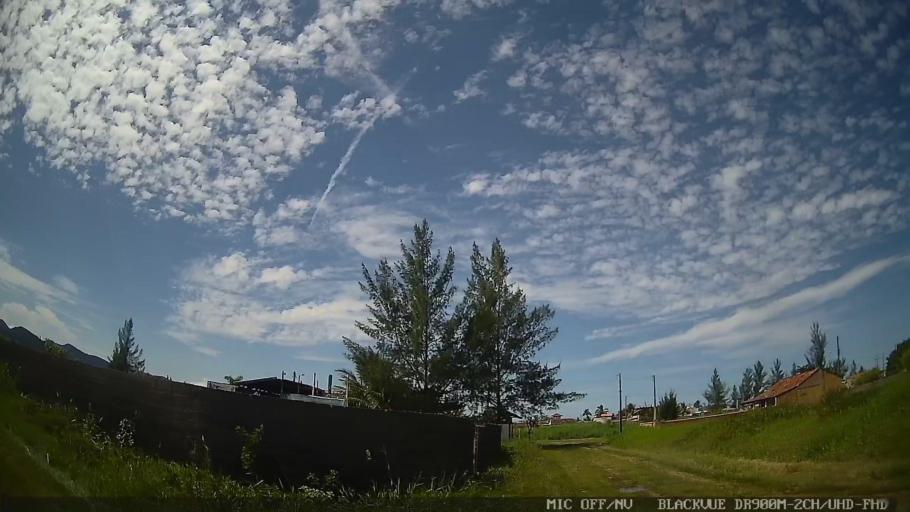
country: BR
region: Sao Paulo
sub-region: Iguape
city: Iguape
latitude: -24.7255
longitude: -47.5130
